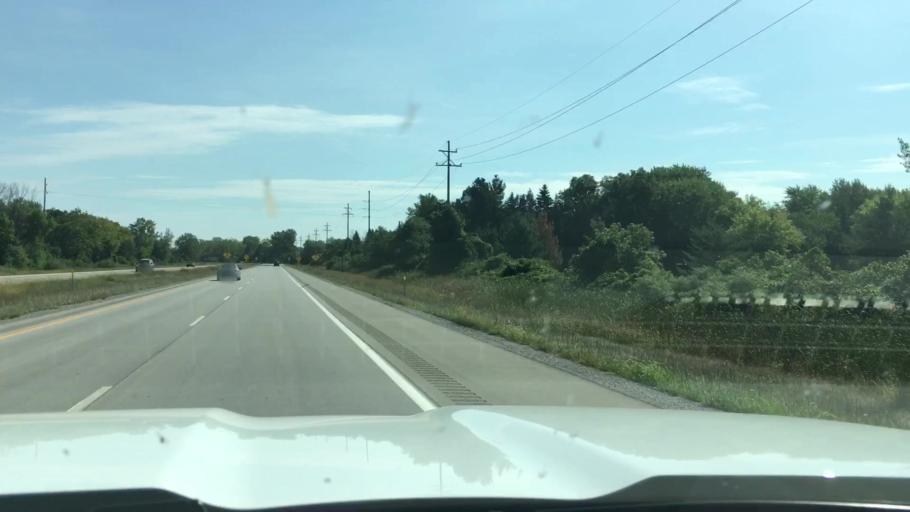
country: US
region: Michigan
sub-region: Bay County
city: Bay City
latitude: 43.5965
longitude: -83.9351
